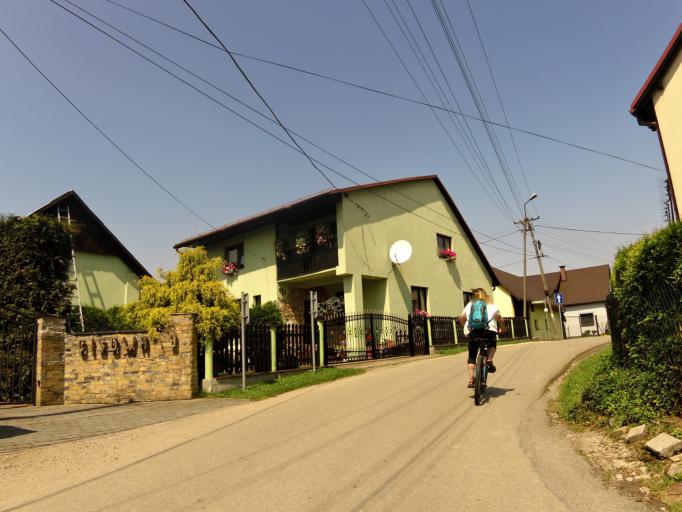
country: PL
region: Silesian Voivodeship
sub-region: Powiat zywiecki
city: Milowka
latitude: 49.5730
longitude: 19.0924
